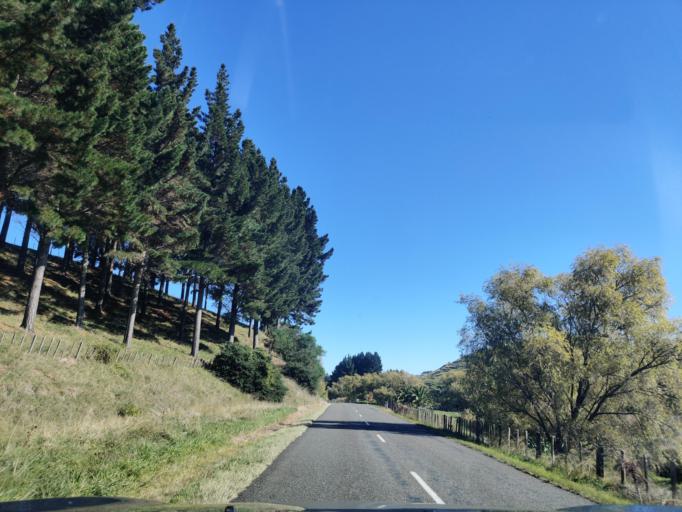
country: NZ
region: Manawatu-Wanganui
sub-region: Palmerston North City
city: Palmerston North
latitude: -40.2571
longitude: 175.7020
